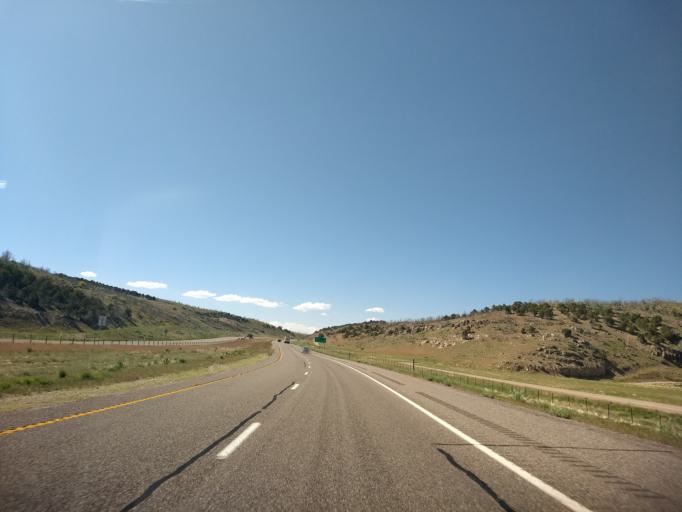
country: US
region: Utah
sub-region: Millard County
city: Fillmore
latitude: 38.6735
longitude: -112.5898
